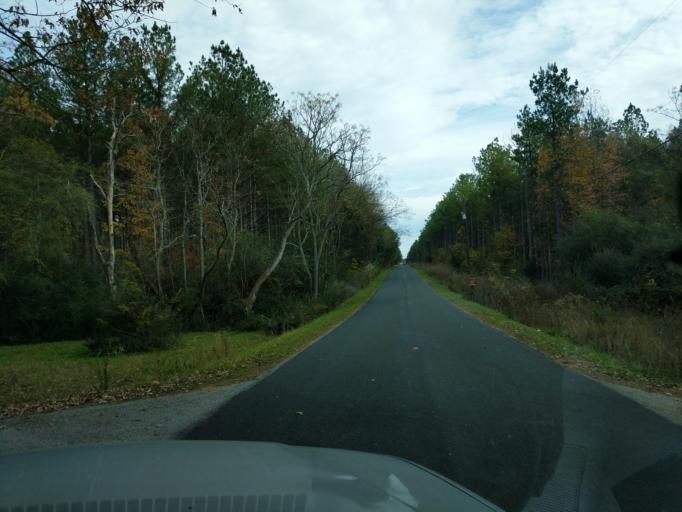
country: US
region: South Carolina
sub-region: Laurens County
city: Watts Mills
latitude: 34.5365
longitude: -81.9261
